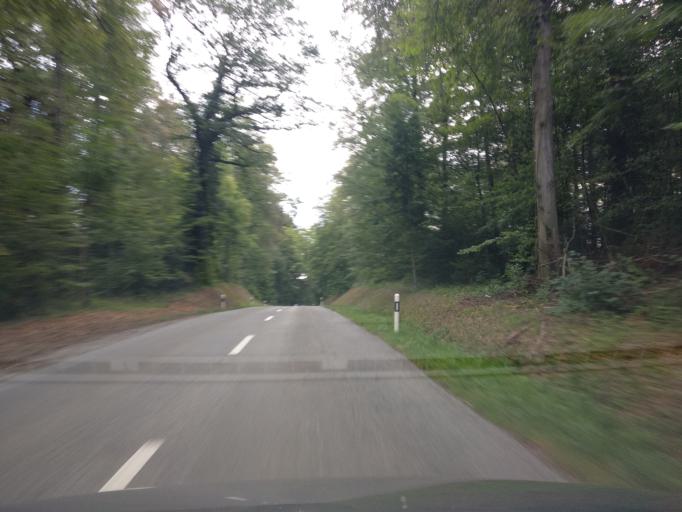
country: CH
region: Thurgau
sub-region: Frauenfeld District
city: Diessenhofen
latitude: 47.6788
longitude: 8.7241
